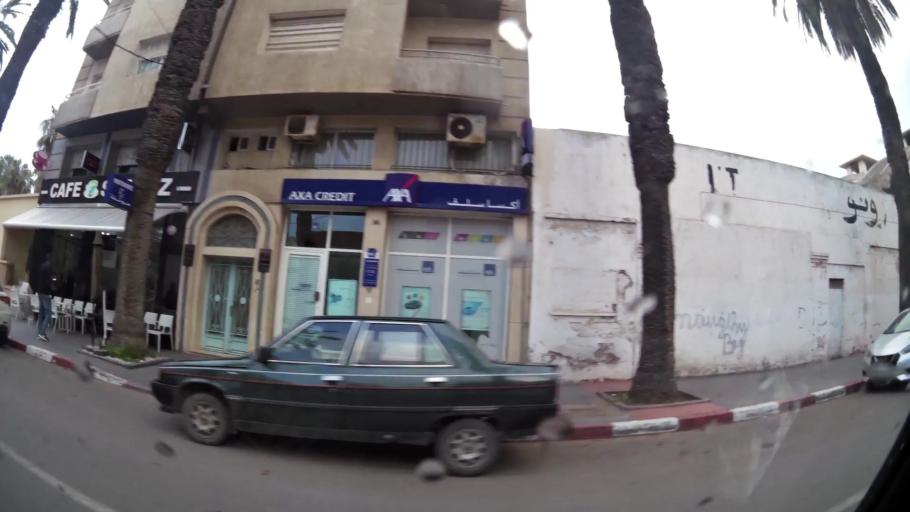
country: MA
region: Doukkala-Abda
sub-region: El-Jadida
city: El Jadida
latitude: 33.2491
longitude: -8.4997
